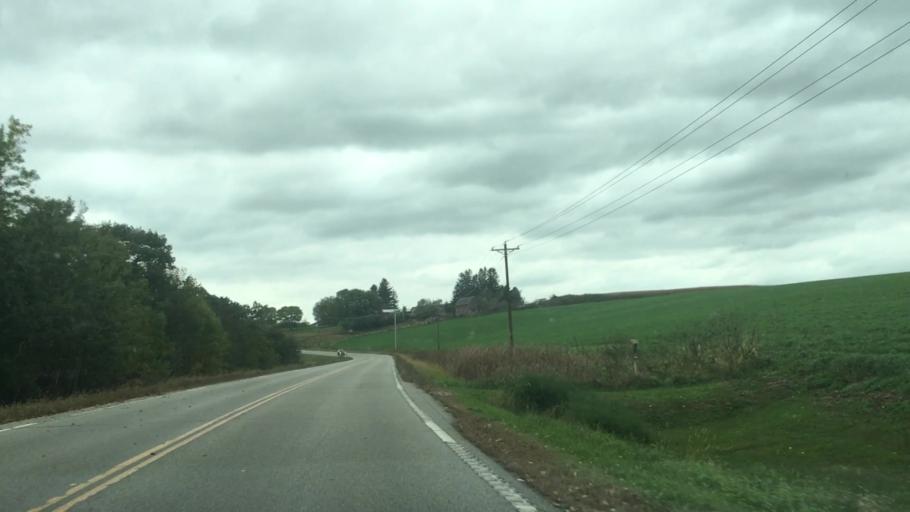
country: US
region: Minnesota
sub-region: Fillmore County
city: Preston
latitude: 43.7351
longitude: -92.0204
